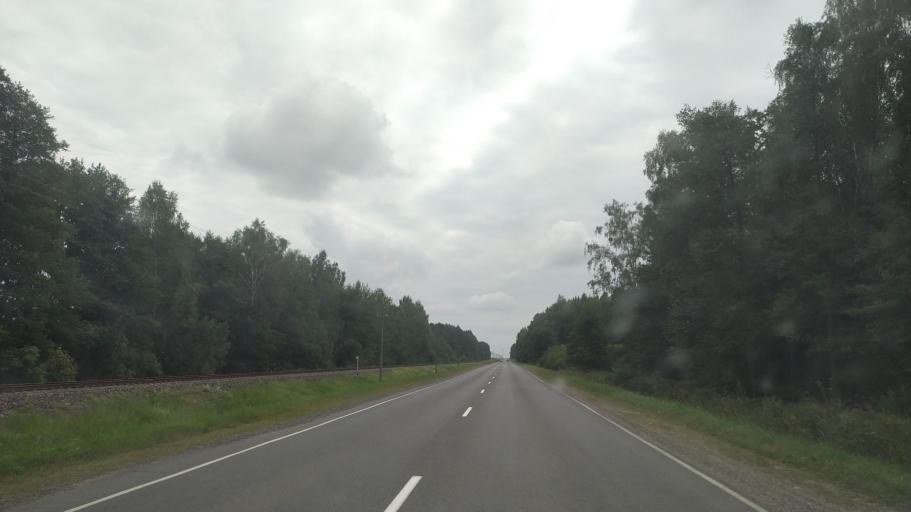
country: BY
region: Brest
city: Byelaazyorsk
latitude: 52.5319
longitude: 25.1434
